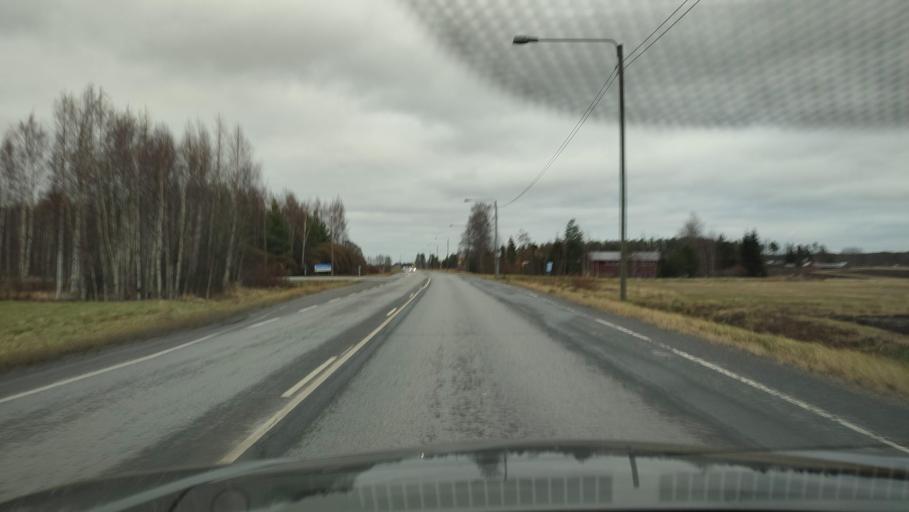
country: FI
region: Southern Ostrobothnia
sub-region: Seinaejoki
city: Kurikka
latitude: 62.6819
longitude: 22.4803
